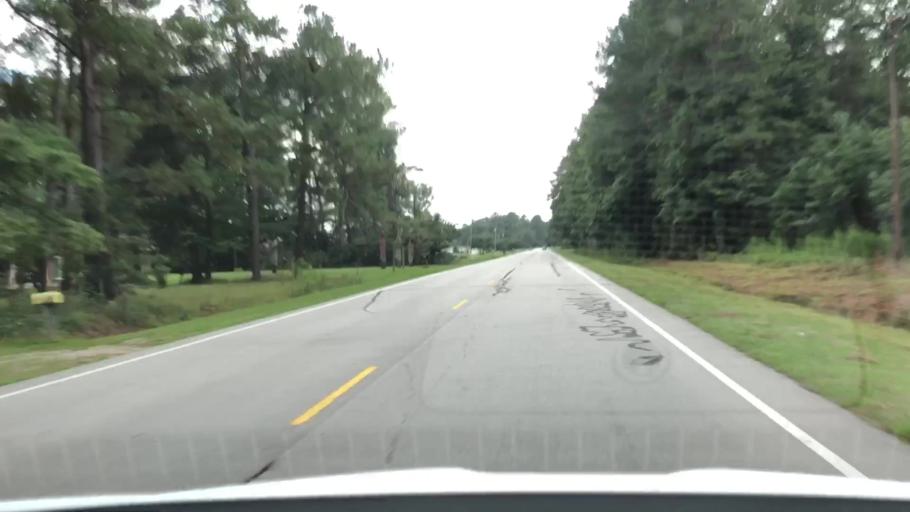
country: US
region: North Carolina
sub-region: Lenoir County
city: Kinston
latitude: 35.1164
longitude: -77.5124
